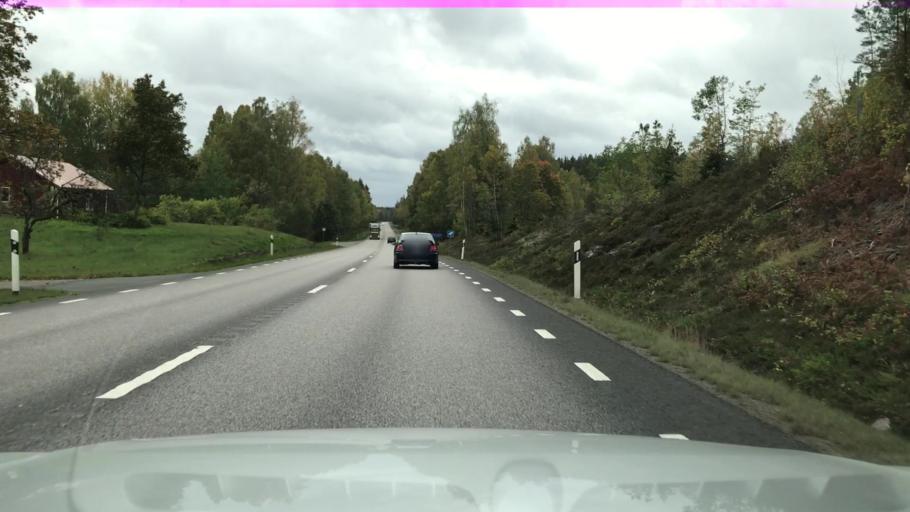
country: SE
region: Kalmar
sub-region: Hultsfreds Kommun
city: Hultsfred
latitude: 57.5522
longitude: 15.8451
